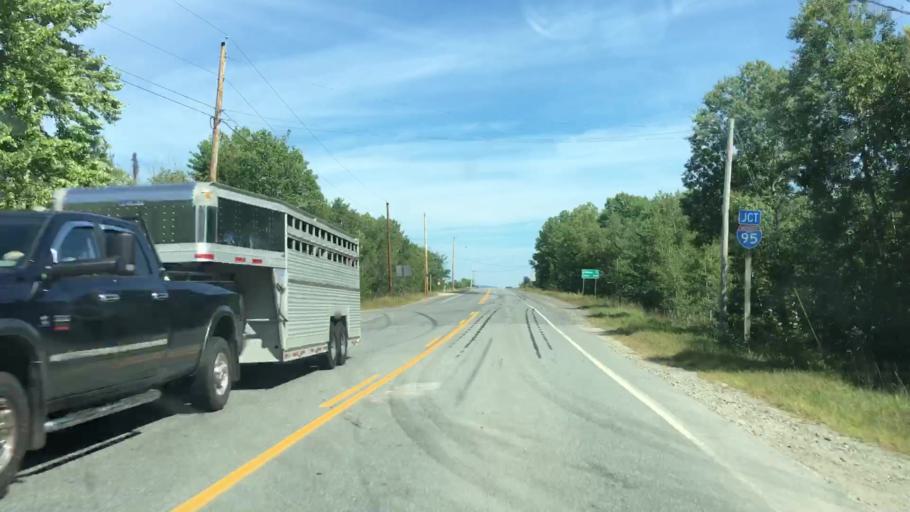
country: US
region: Maine
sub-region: Penobscot County
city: Howland
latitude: 45.2349
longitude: -68.6829
